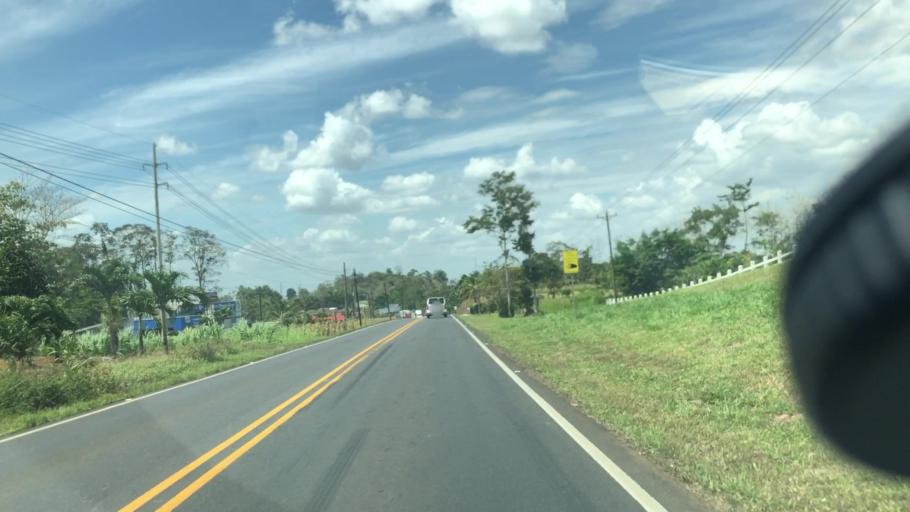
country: CR
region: Alajuela
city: Pital
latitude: 10.4563
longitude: -84.3862
